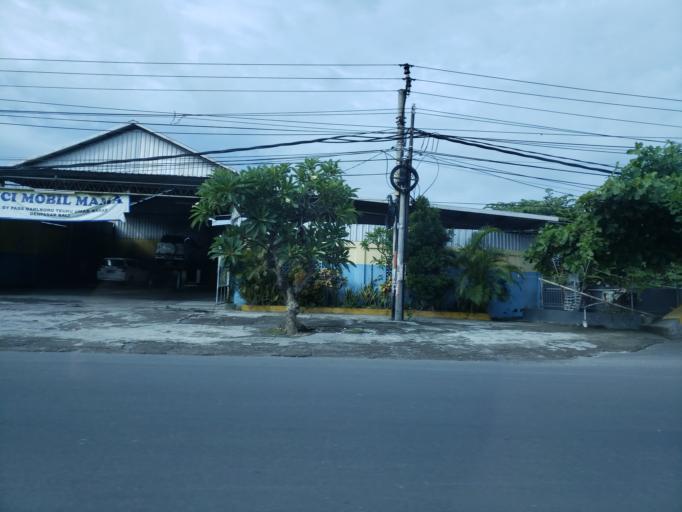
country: ID
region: Bali
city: Denpasar
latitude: -8.6775
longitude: 115.1863
